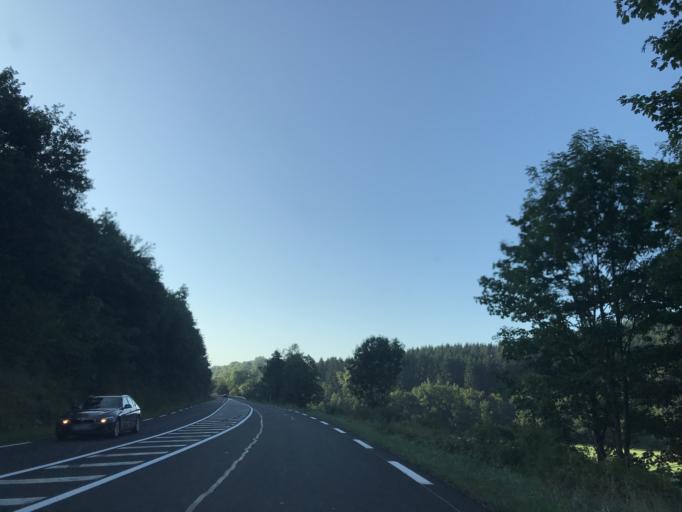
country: FR
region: Auvergne
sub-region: Departement du Puy-de-Dome
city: Job
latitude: 45.5988
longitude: 3.7212
